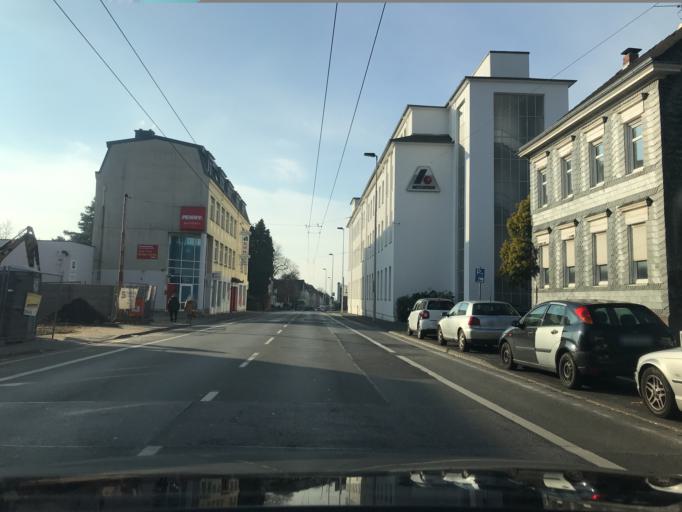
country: DE
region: North Rhine-Westphalia
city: Haan
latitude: 51.1714
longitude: 7.0178
